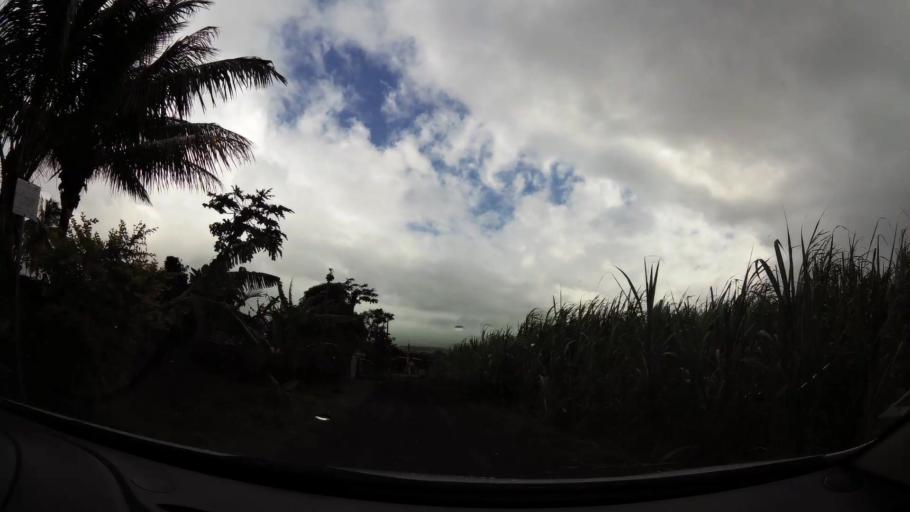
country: RE
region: Reunion
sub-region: Reunion
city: Saint-Andre
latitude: -20.9280
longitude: 55.6436
